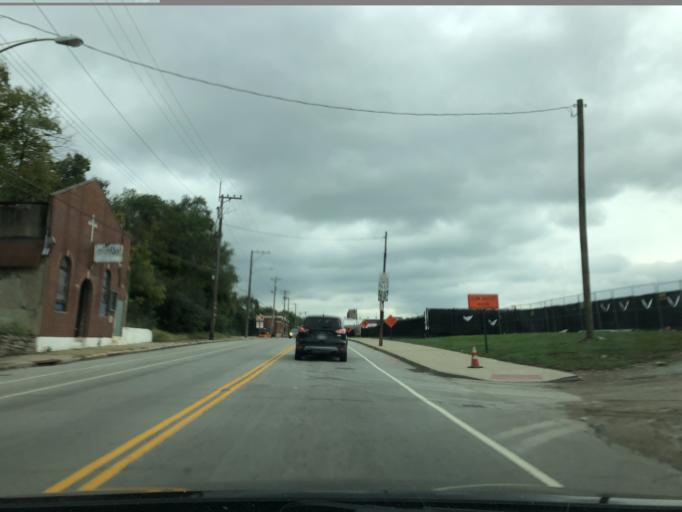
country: US
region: Kentucky
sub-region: Campbell County
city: Dayton
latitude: 39.1231
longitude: -84.4561
